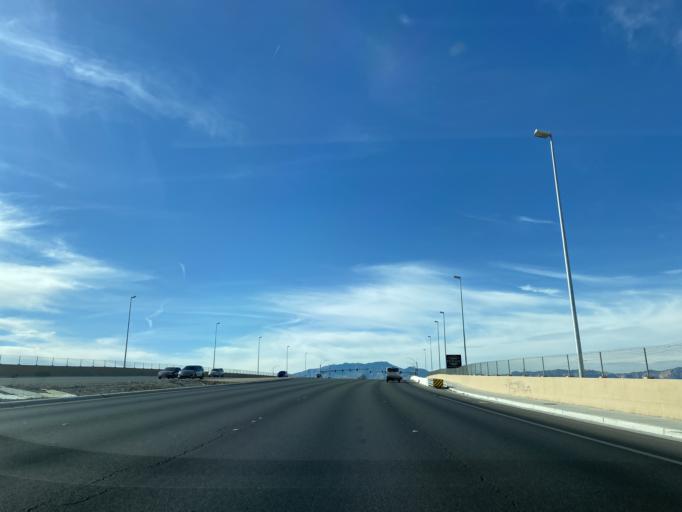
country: US
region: Nevada
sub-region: Clark County
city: Enterprise
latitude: 36.0263
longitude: -115.2225
